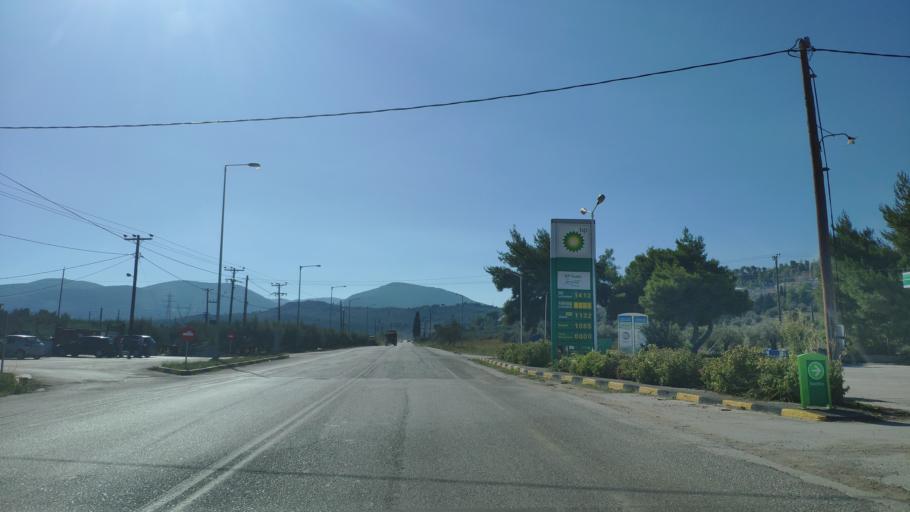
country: GR
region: Peloponnese
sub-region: Nomos Korinthias
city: Athikia
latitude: 37.8473
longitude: 22.8983
